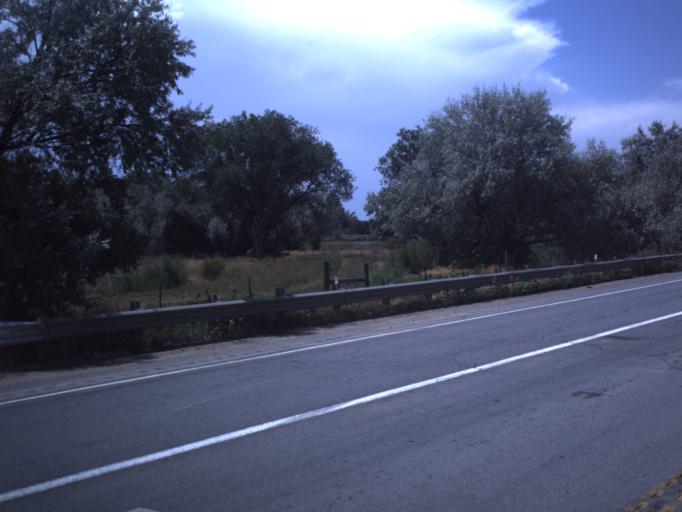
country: US
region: Utah
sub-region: Duchesne County
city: Roosevelt
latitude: 40.3020
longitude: -109.8405
